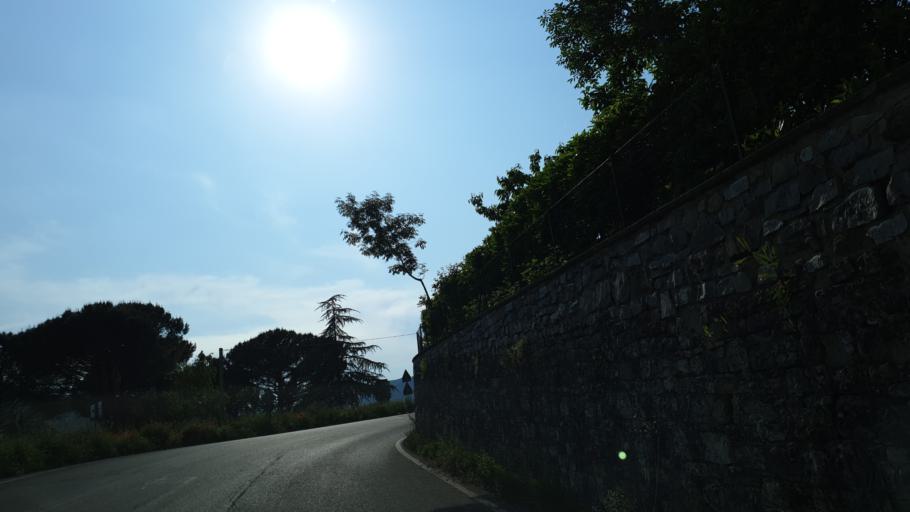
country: IT
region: Tuscany
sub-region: Province of Arezzo
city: Strada
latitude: 43.7432
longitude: 11.7359
